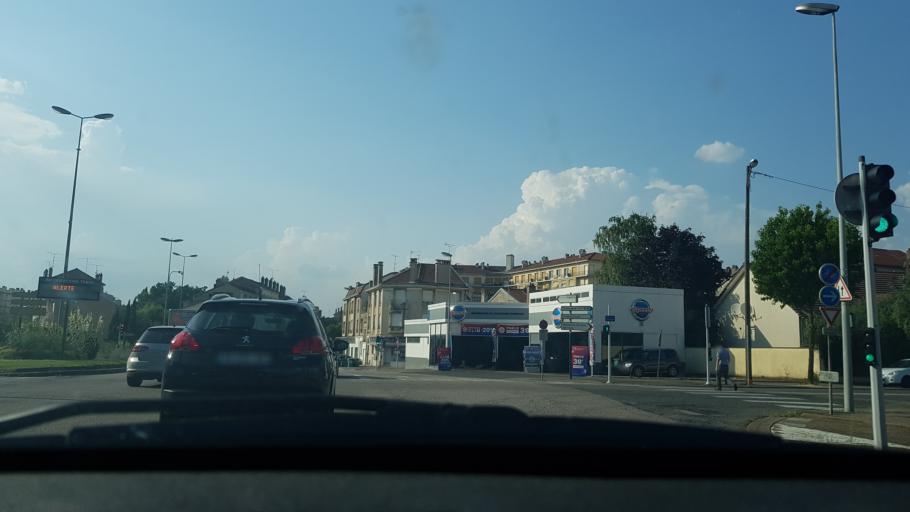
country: FR
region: Lorraine
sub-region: Departement de Meurthe-et-Moselle
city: Nancy
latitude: 48.6731
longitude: 6.1841
